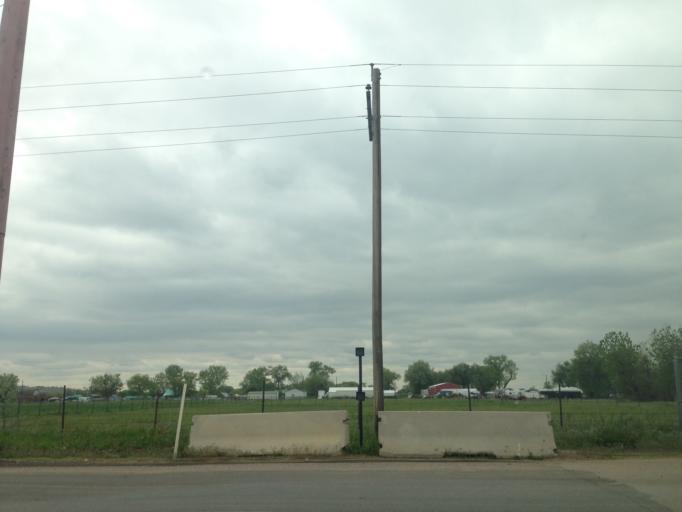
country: US
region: Colorado
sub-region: Boulder County
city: Gunbarrel
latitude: 40.0440
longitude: -105.1834
